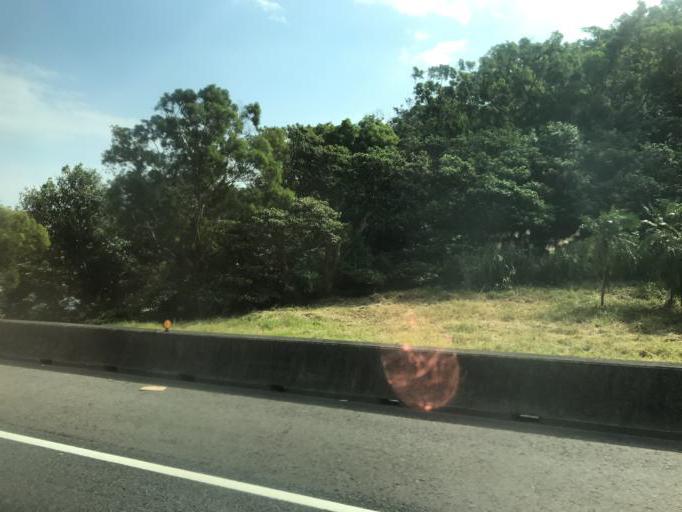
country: TW
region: Taiwan
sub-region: Hsinchu
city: Zhubei
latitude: 24.8764
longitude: 121.0493
